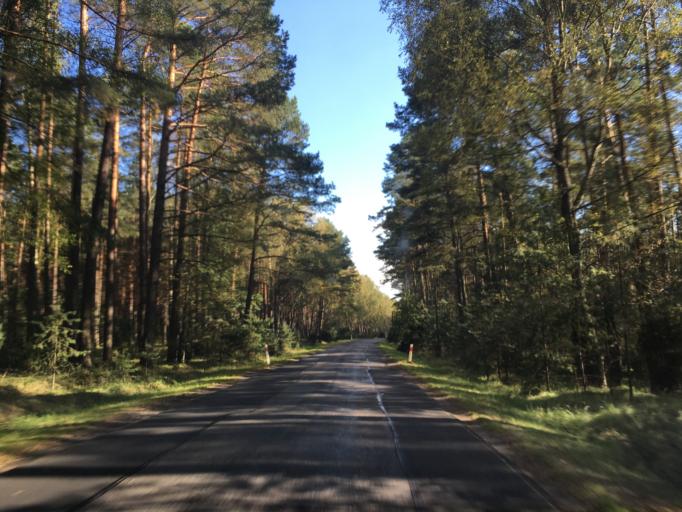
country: PL
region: Kujawsko-Pomorskie
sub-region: Powiat swiecki
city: Warlubie
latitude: 53.6111
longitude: 18.5434
